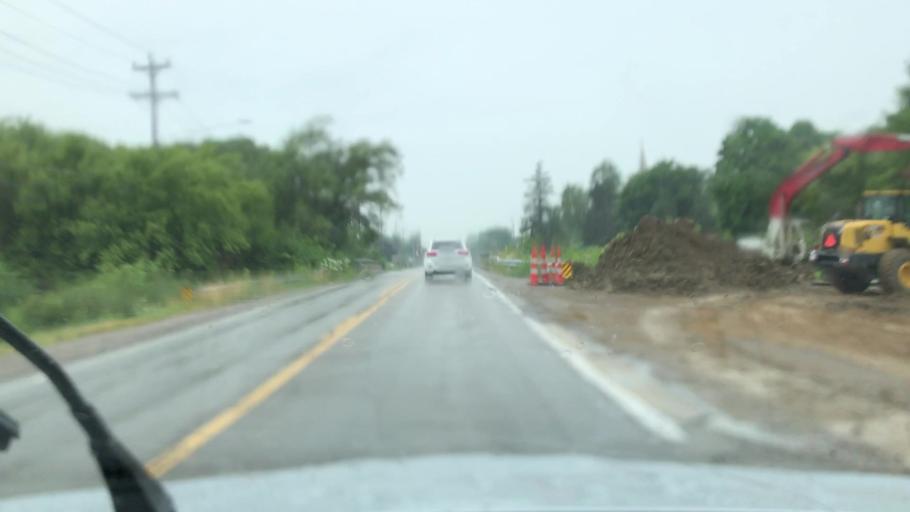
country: US
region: Michigan
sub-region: Macomb County
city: Clinton
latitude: 42.6429
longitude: -82.9325
